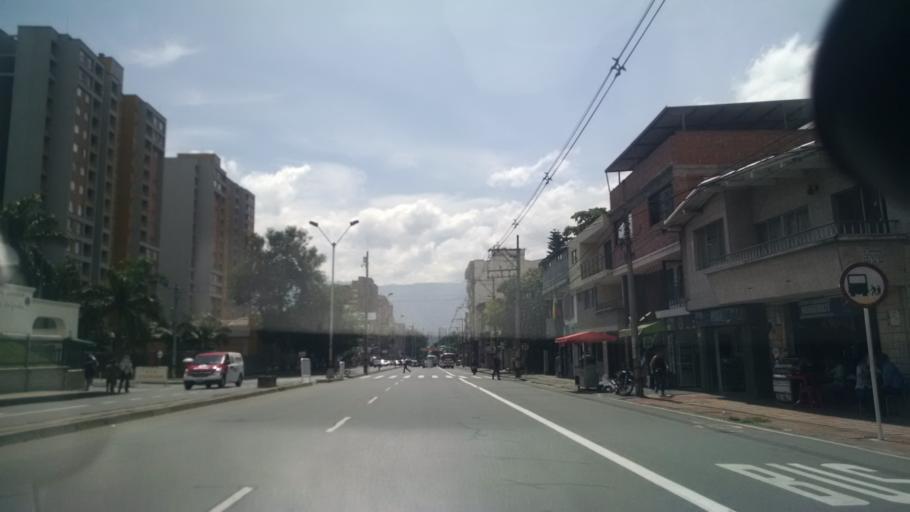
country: CO
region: Antioquia
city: Medellin
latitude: 6.2611
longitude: -75.5915
